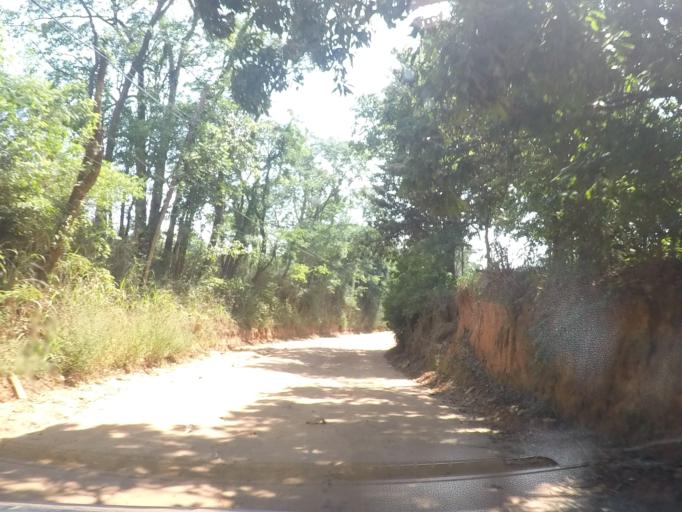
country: BR
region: Sao Paulo
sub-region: Monte Mor
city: Monte Mor
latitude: -22.8862
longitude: -47.2972
